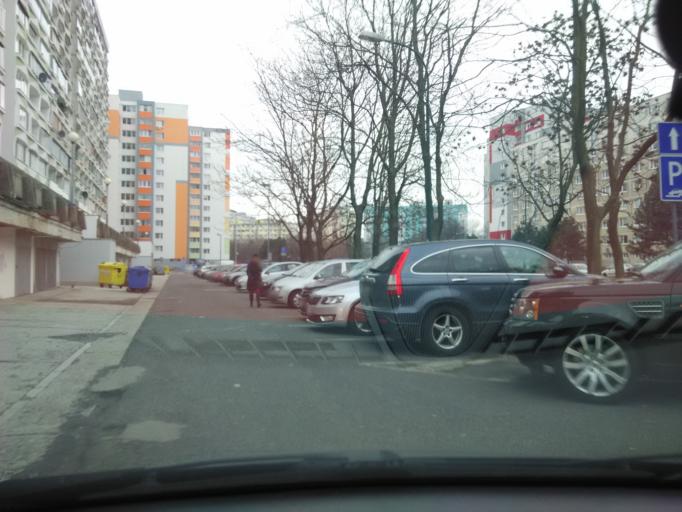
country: AT
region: Burgenland
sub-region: Politischer Bezirk Neusiedl am See
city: Kittsee
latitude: 48.1026
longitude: 17.1057
